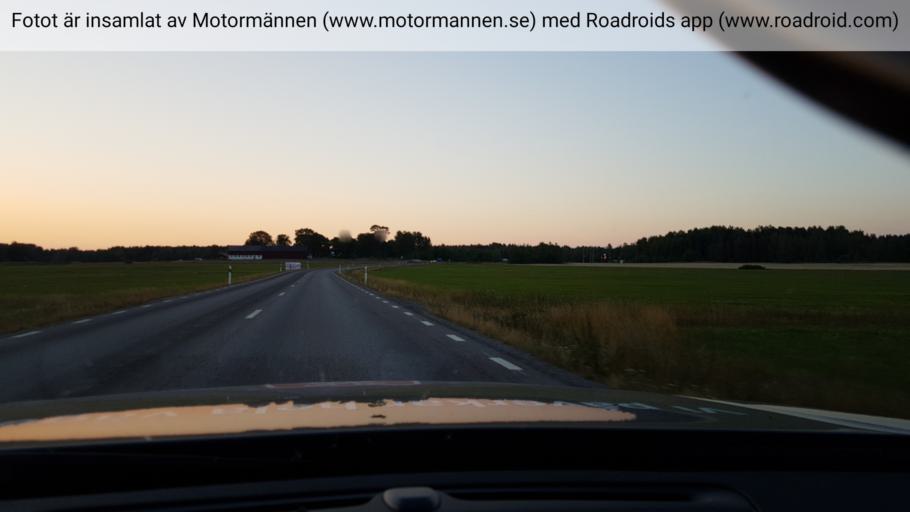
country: SE
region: Uppsala
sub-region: Heby Kommun
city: OEstervala
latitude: 60.0941
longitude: 17.1878
